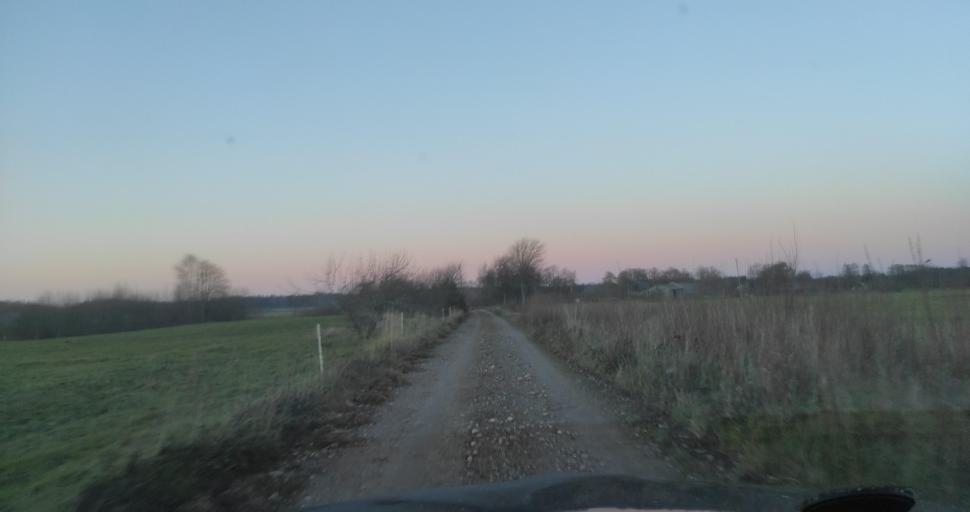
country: LV
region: Dundaga
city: Dundaga
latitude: 57.3724
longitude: 22.2253
